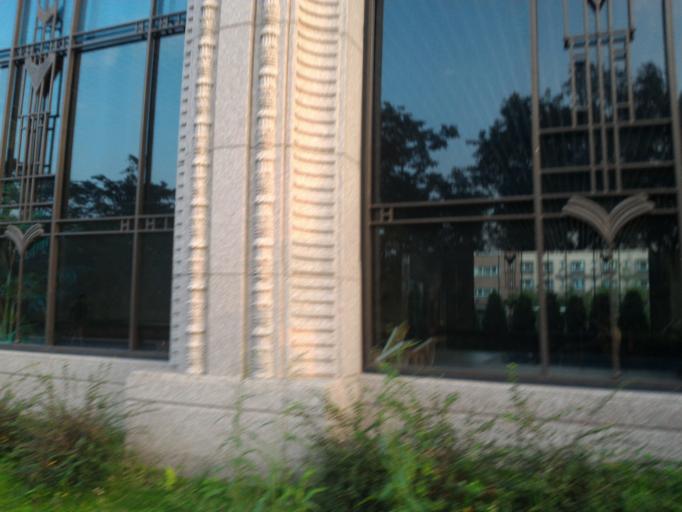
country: TW
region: Taiwan
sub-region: Taoyuan
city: Taoyuan
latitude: 24.9506
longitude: 121.3800
